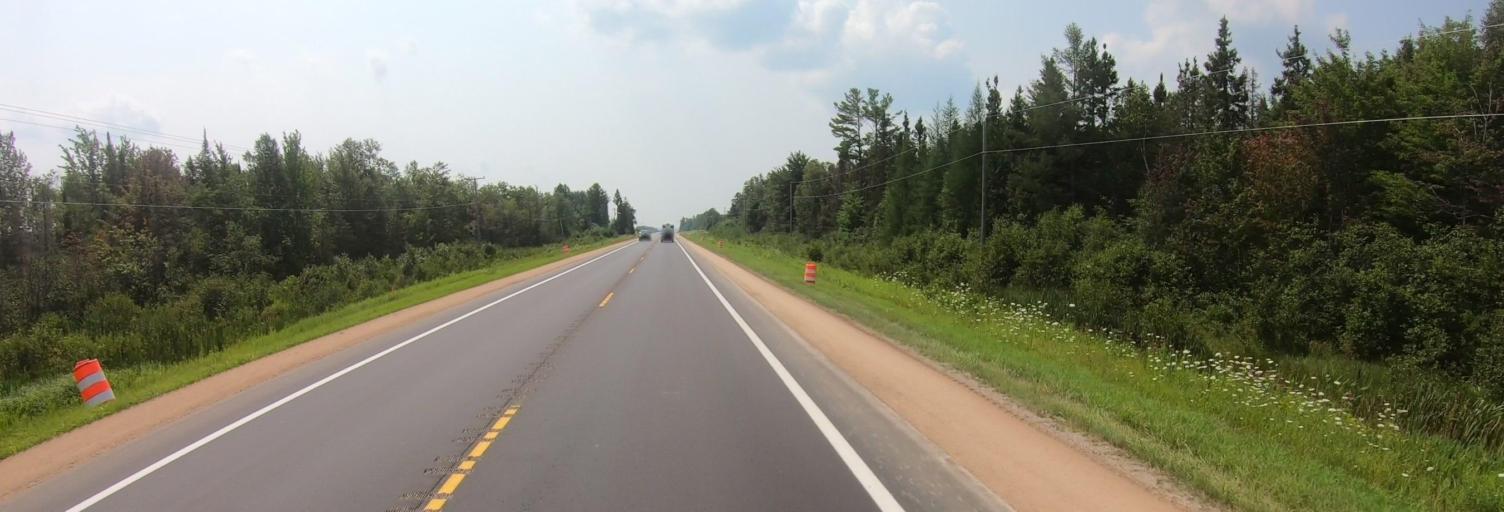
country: US
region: Michigan
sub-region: Luce County
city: Newberry
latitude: 46.4072
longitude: -85.5100
